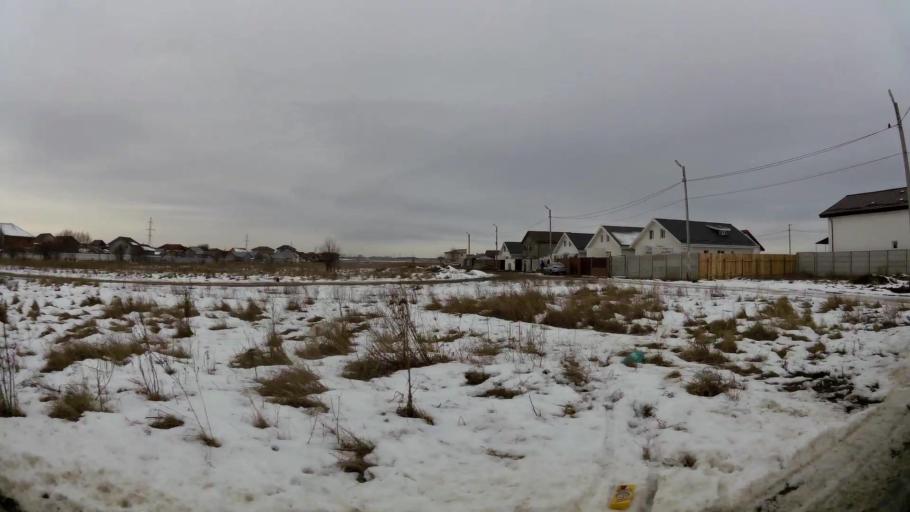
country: RO
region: Ilfov
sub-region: Comuna Pantelimon
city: Pantelimon
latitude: 44.4638
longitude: 26.2041
